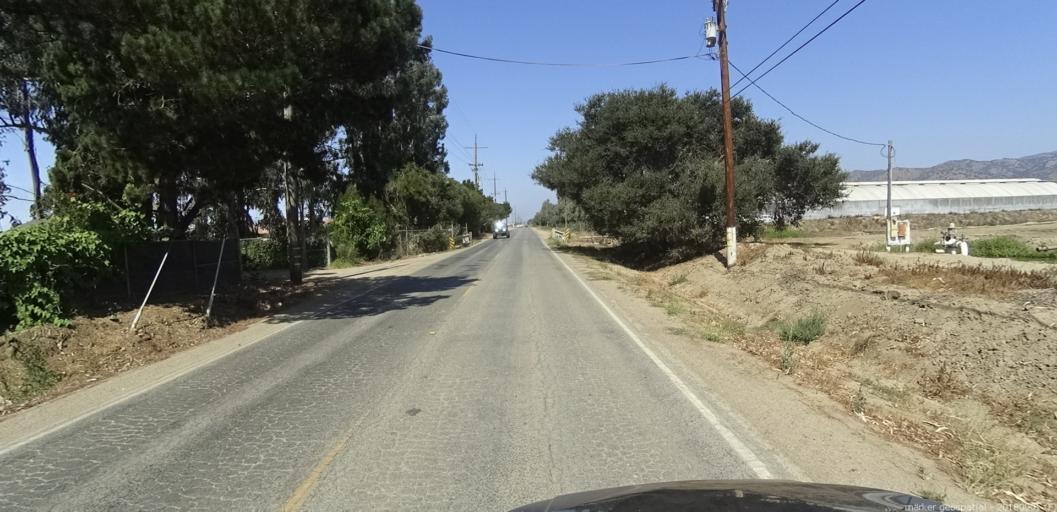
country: US
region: California
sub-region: Monterey County
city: Chualar
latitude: 36.6164
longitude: -121.5225
